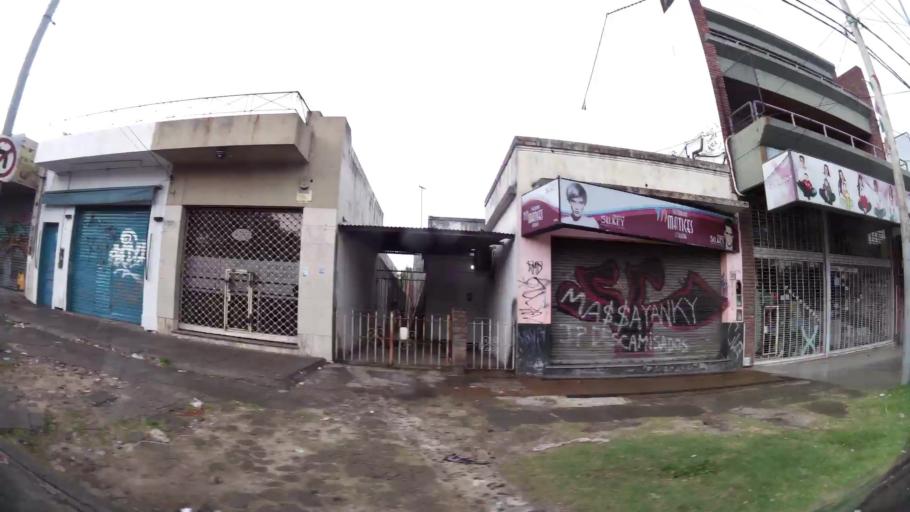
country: AR
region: Buenos Aires
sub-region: Partido de Quilmes
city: Quilmes
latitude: -34.7642
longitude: -58.2138
